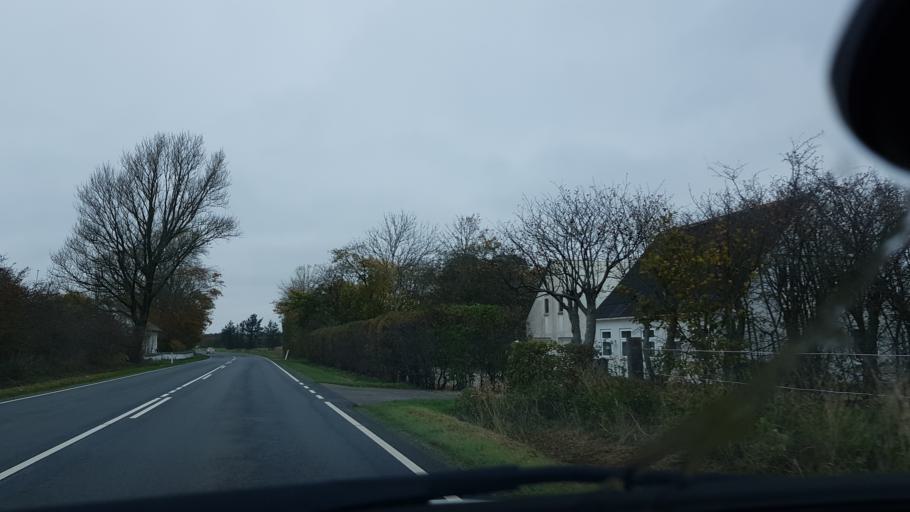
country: DK
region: South Denmark
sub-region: Esbjerg Kommune
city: Ribe
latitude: 55.2740
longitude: 8.8670
